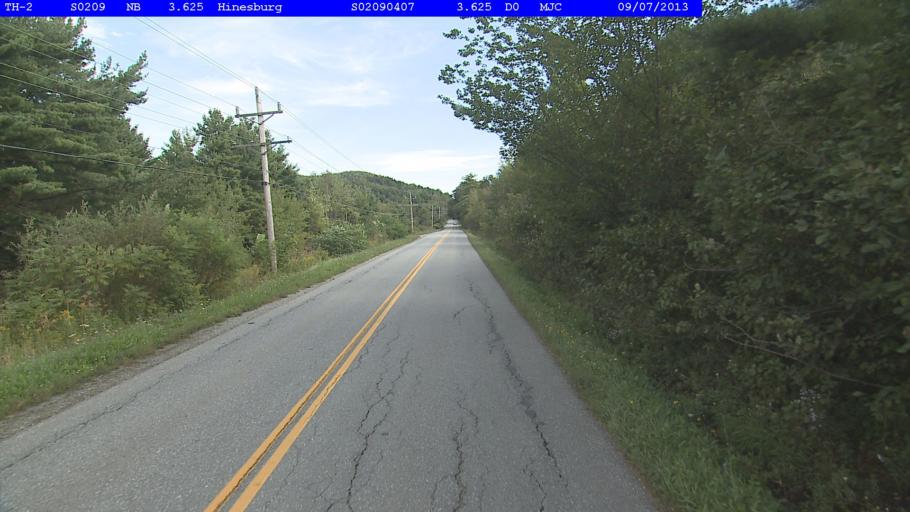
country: US
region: Vermont
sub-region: Chittenden County
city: Hinesburg
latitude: 44.3630
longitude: -73.0725
